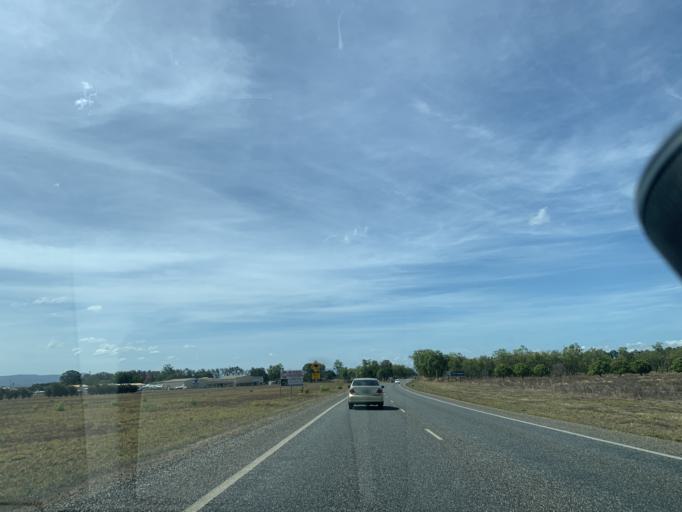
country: AU
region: Queensland
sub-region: Tablelands
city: Mareeba
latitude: -17.0746
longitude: 145.4352
